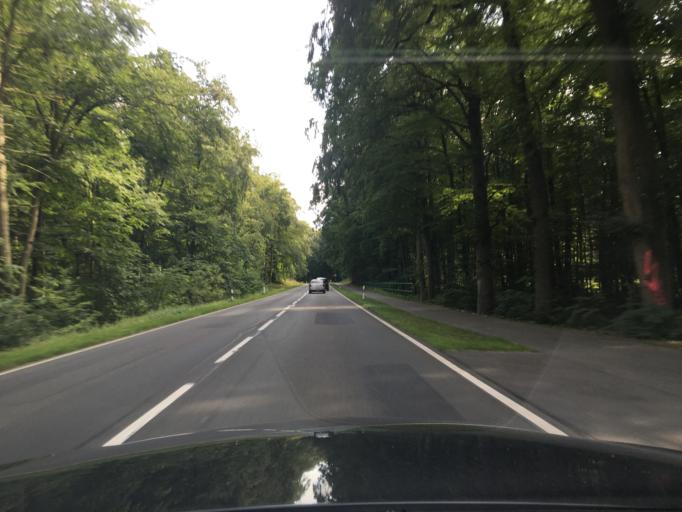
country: DE
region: Mecklenburg-Vorpommern
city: Neustrelitz
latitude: 53.4205
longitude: 13.0421
